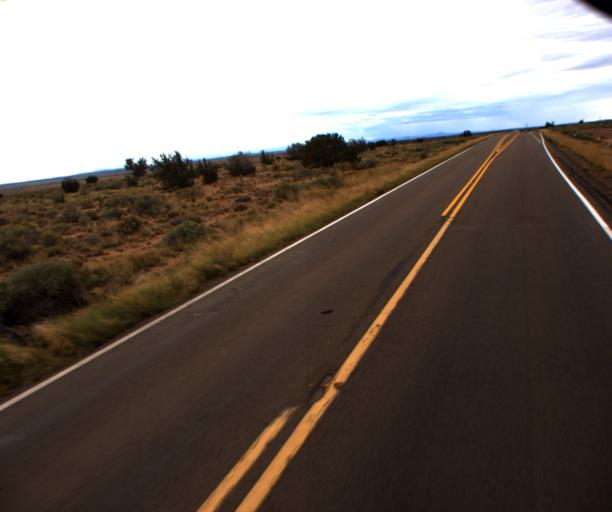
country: US
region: Arizona
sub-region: Navajo County
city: Snowflake
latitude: 34.6799
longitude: -110.1038
